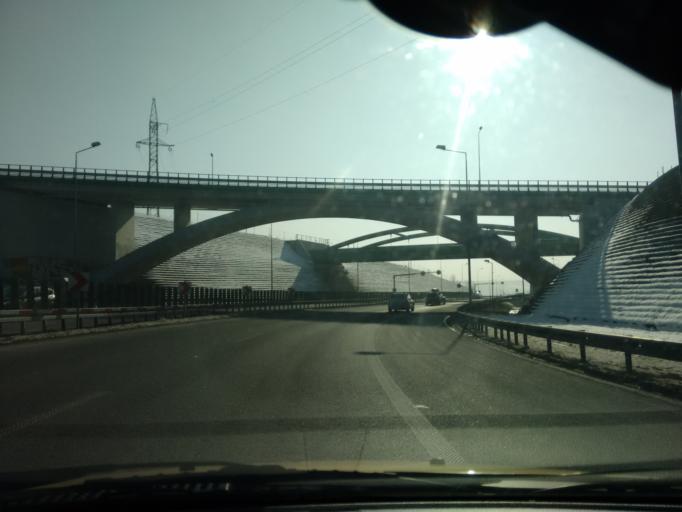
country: PL
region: Silesian Voivodeship
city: Janowice
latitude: 49.8421
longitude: 19.0902
